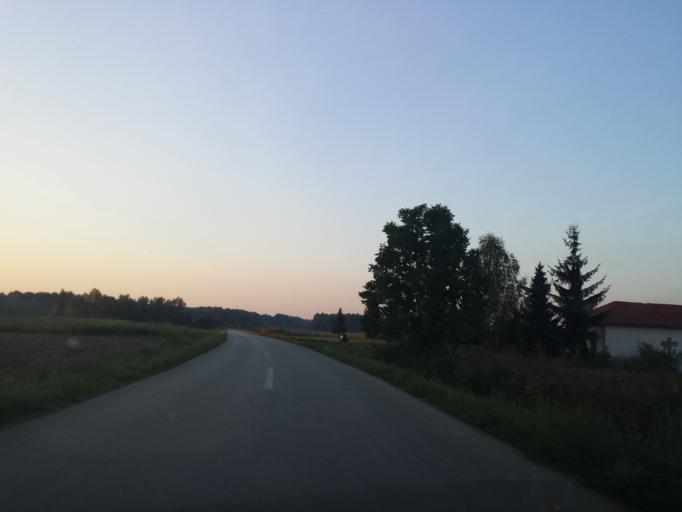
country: HR
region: Brodsko-Posavska
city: Oriovac
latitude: 45.1047
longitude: 17.8291
